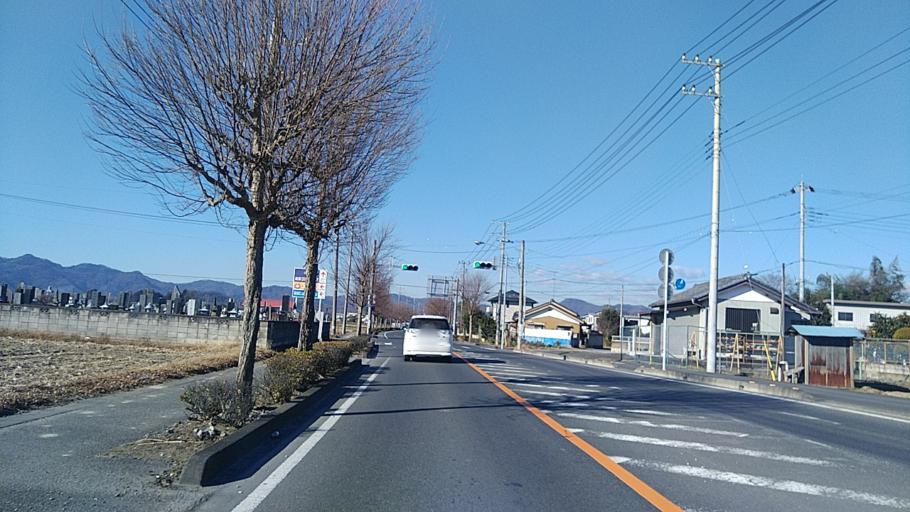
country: JP
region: Tochigi
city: Tanuma
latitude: 36.3450
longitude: 139.5678
